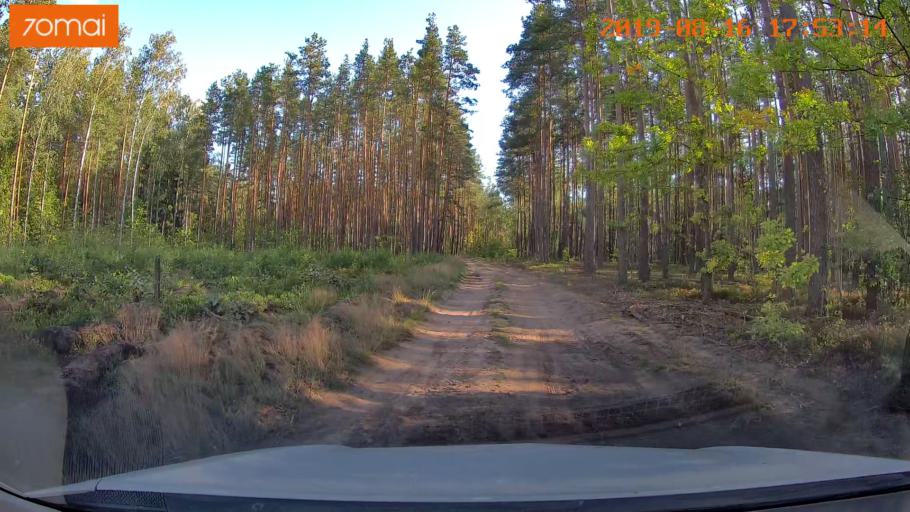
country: BY
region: Mogilev
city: Asipovichy
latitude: 53.2252
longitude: 28.6589
